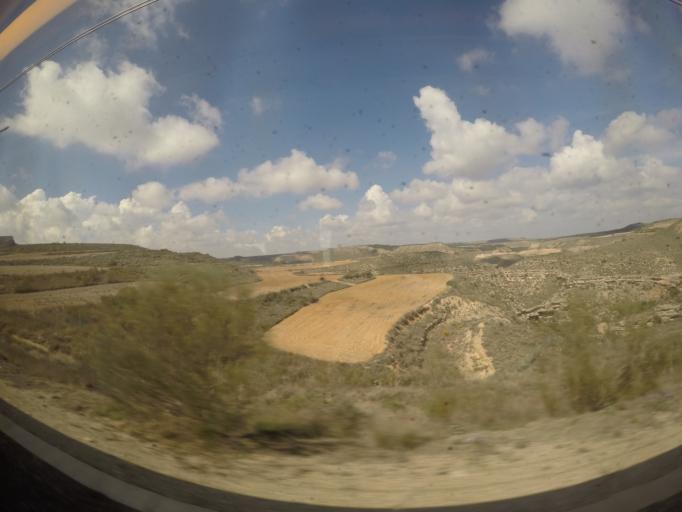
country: ES
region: Aragon
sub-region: Provincia de Huesca
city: Valfarta
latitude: 41.5263
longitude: -0.1256
